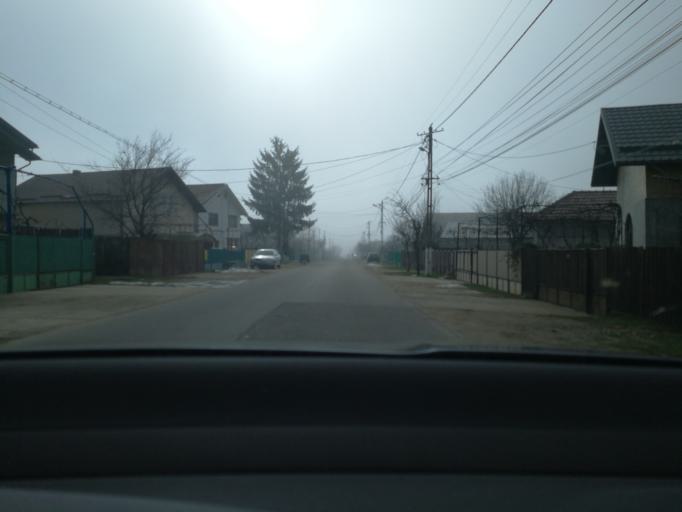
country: RO
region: Prahova
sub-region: Comuna Magureni
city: Lunca Prahovei
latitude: 45.0339
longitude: 25.7636
